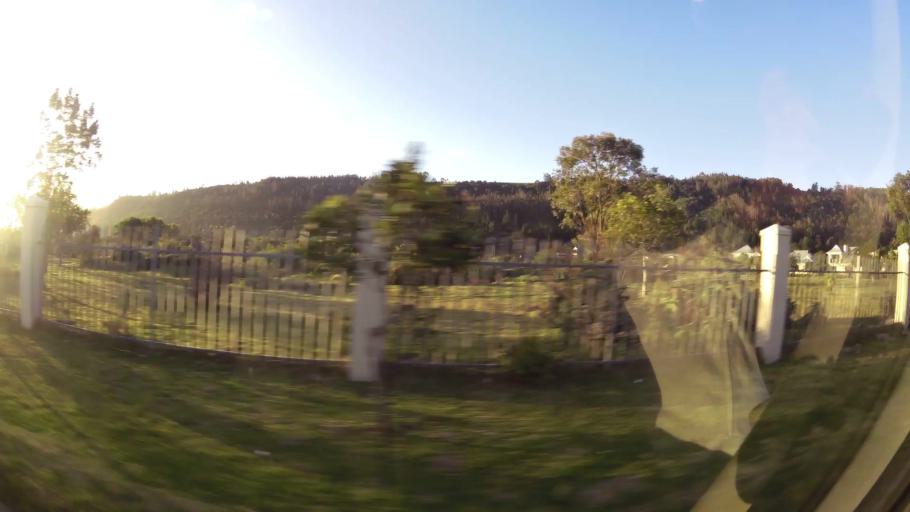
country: ZA
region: Western Cape
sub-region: Eden District Municipality
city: Knysna
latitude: -34.0124
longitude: 22.7910
